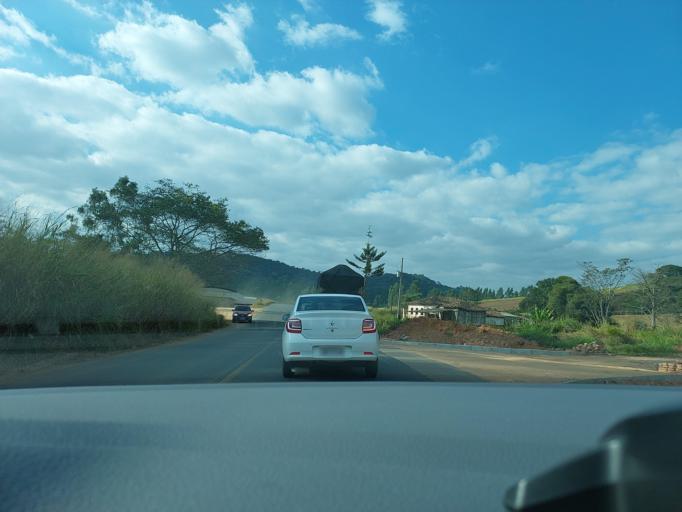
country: BR
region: Minas Gerais
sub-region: Vicosa
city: Vicosa
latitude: -20.8307
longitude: -42.7854
